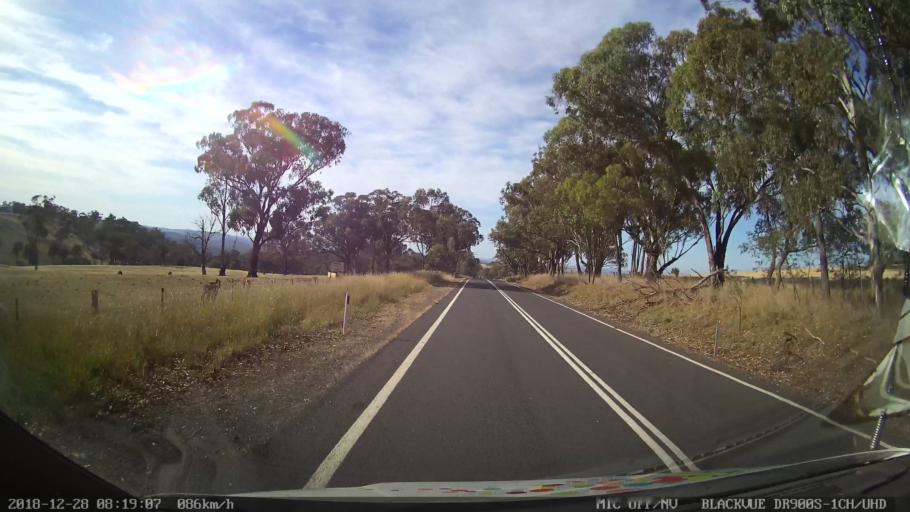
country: AU
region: New South Wales
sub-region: Blayney
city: Blayney
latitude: -33.8549
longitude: 149.3510
